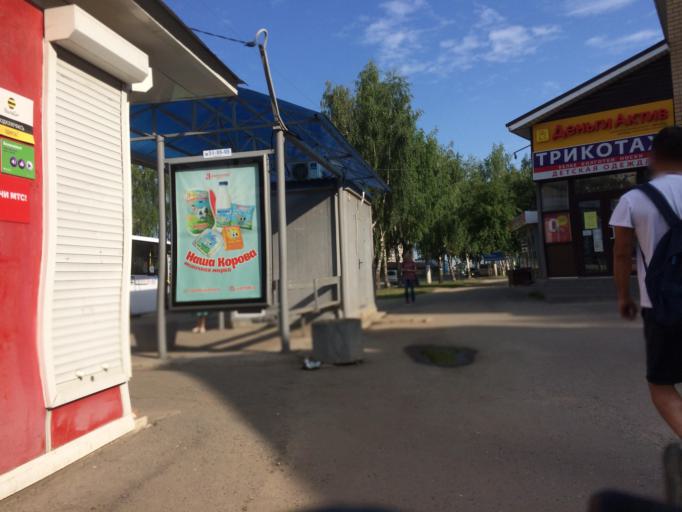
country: RU
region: Mariy-El
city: Medvedevo
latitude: 56.6389
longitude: 47.8327
